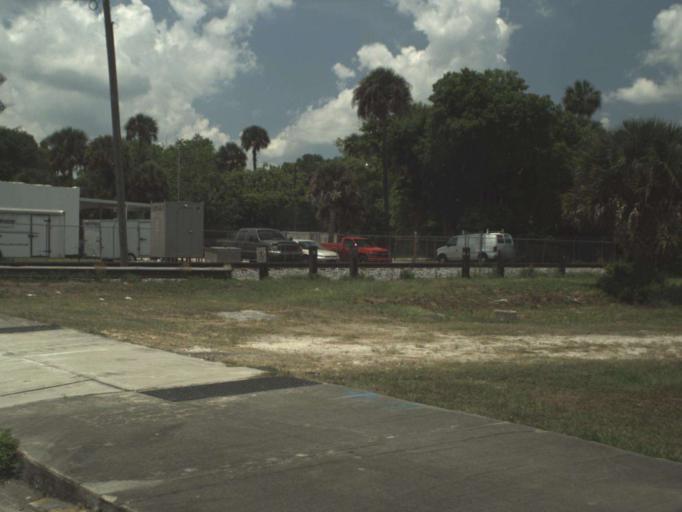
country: US
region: Florida
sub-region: Volusia County
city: New Smyrna Beach
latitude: 29.0235
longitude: -80.9268
